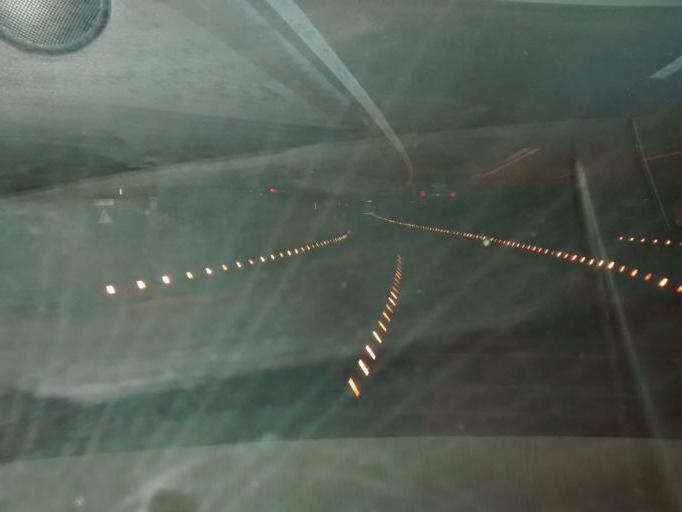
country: ES
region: Catalonia
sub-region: Provincia de Barcelona
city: les Corts
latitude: 41.4047
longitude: 2.1180
